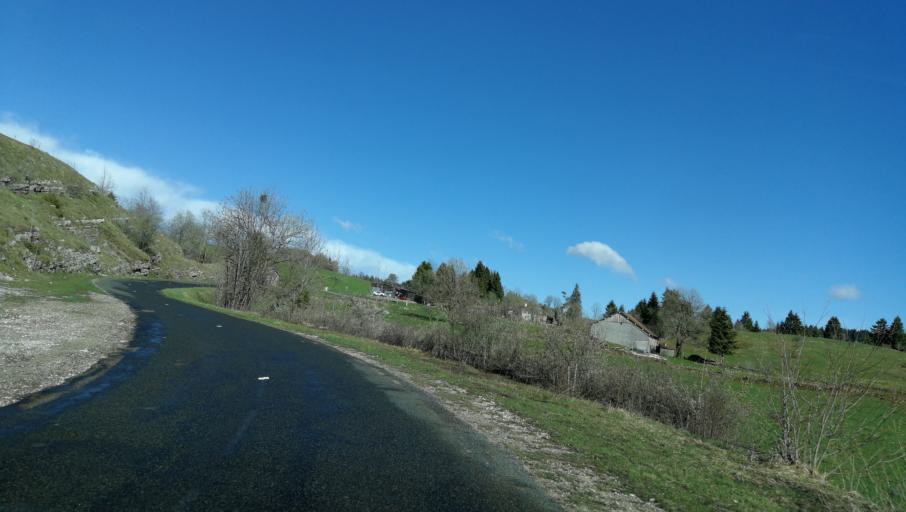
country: FR
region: Franche-Comte
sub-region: Departement du Jura
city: Saint-Claude
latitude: 46.3059
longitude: 5.8371
